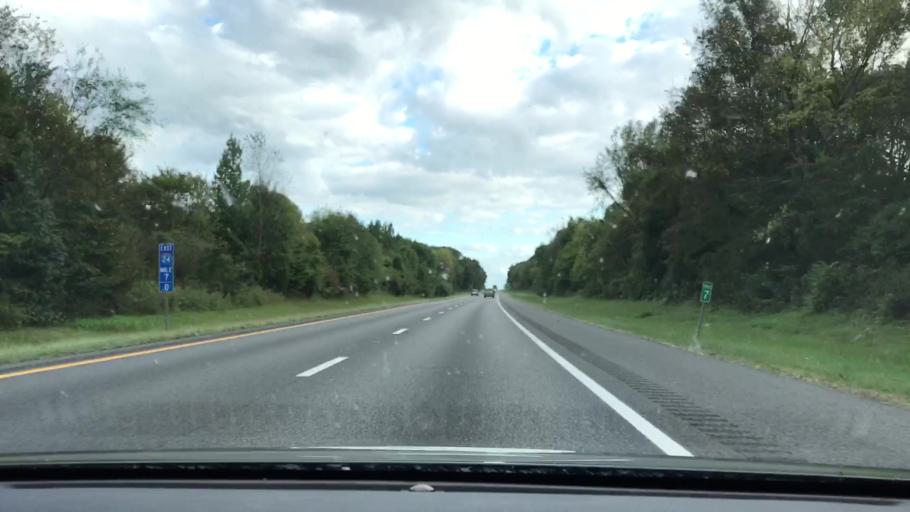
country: US
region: Tennessee
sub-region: Montgomery County
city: Clarksville
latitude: 36.5686
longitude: -87.2566
